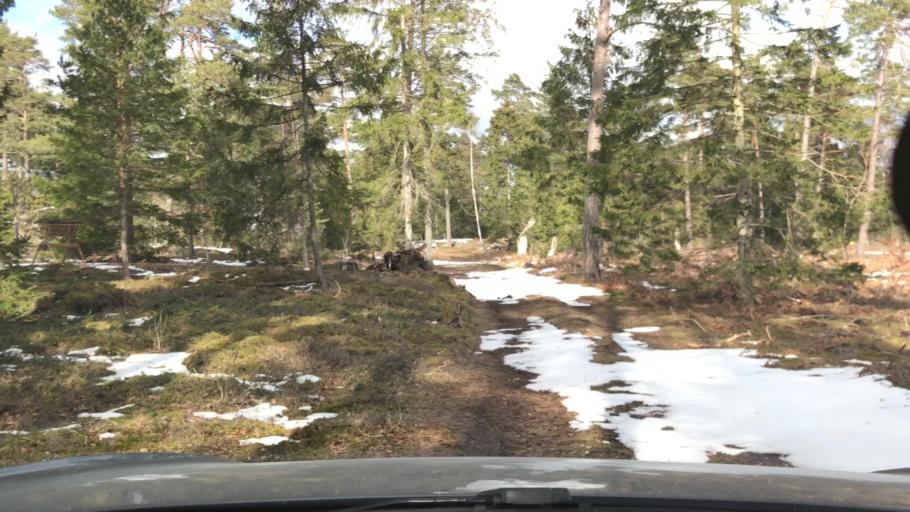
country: SE
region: Gotland
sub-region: Gotland
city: Slite
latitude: 57.3466
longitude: 18.7299
